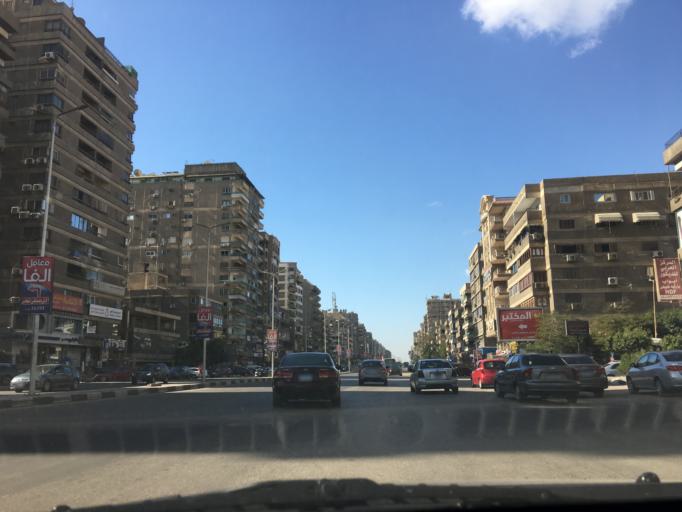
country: EG
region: Muhafazat al Qahirah
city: Cairo
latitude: 30.0547
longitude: 31.3457
